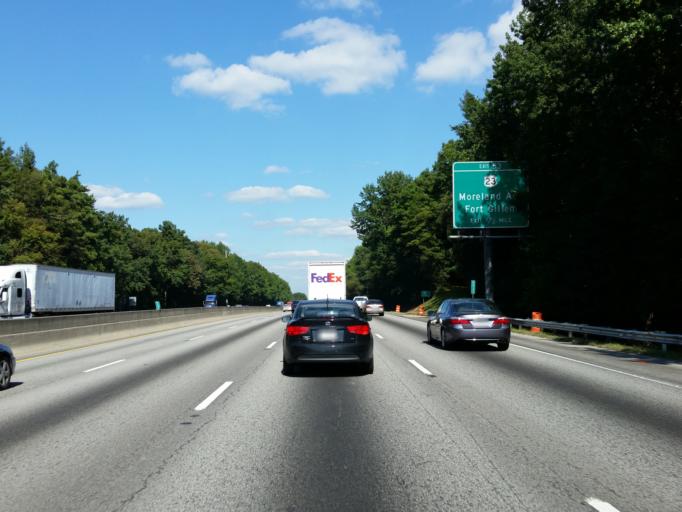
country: US
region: Georgia
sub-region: Clayton County
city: Conley
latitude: 33.6632
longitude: -84.3511
